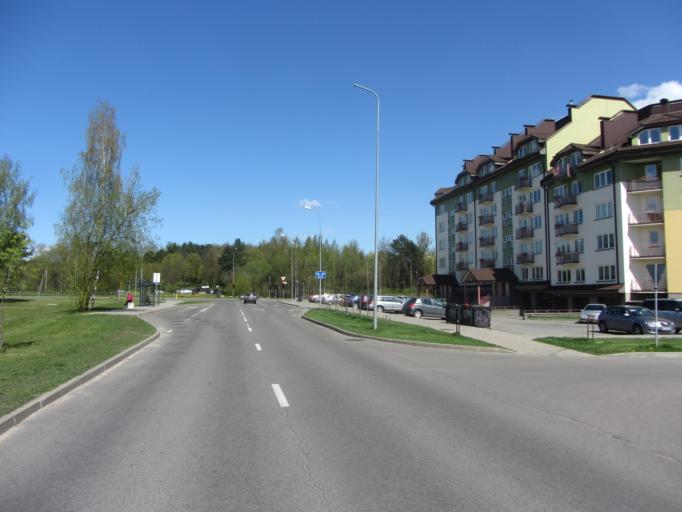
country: LT
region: Vilnius County
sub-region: Vilnius
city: Fabijoniskes
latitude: 54.7522
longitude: 25.2700
